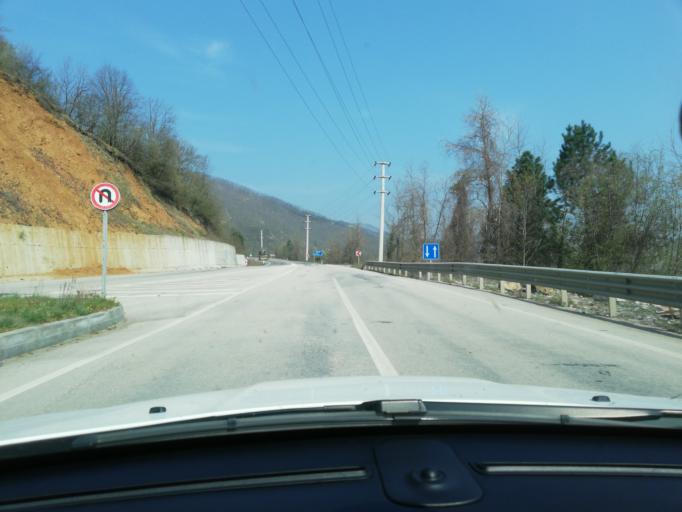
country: TR
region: Karabuk
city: Yenice
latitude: 41.2069
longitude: 32.3647
